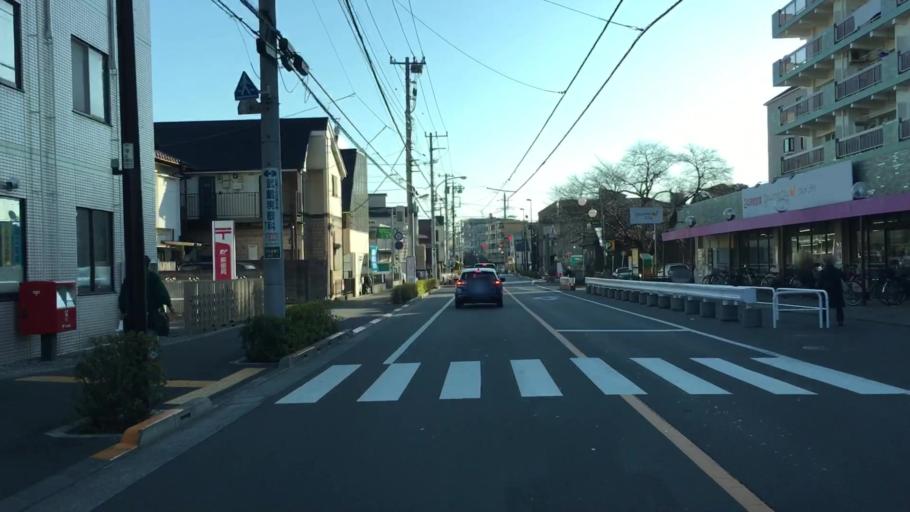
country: JP
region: Tokyo
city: Kamirenjaku
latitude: 35.6994
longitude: 139.5383
